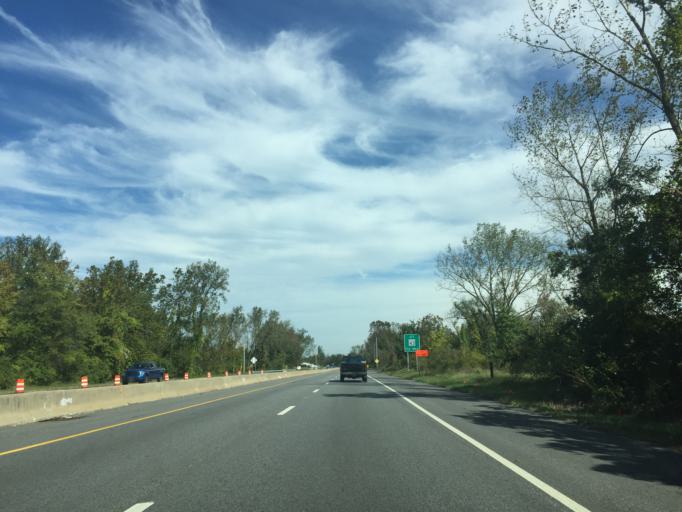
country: US
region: Maryland
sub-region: Baltimore County
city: White Marsh
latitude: 39.3646
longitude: -76.4412
